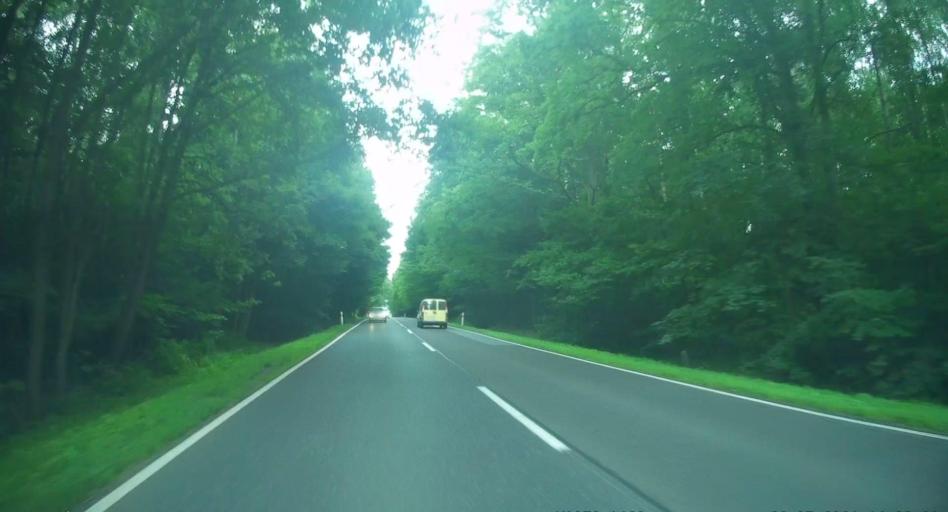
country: PL
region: Lodz Voivodeship
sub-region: Powiat brzezinski
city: Rogow
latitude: 51.8085
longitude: 19.9113
